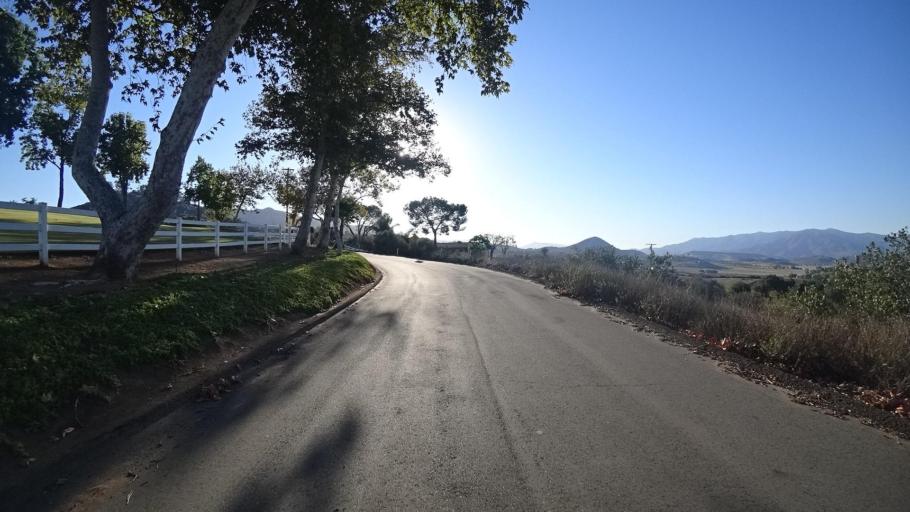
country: US
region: California
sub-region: San Diego County
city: Jamul
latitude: 32.7132
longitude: -116.8630
